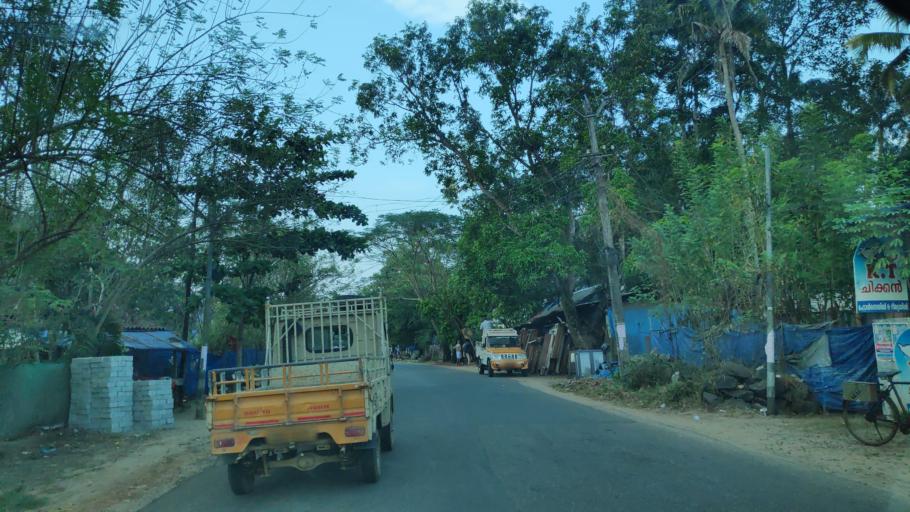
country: IN
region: Kerala
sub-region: Alappuzha
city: Shertallai
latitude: 9.6393
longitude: 76.3716
